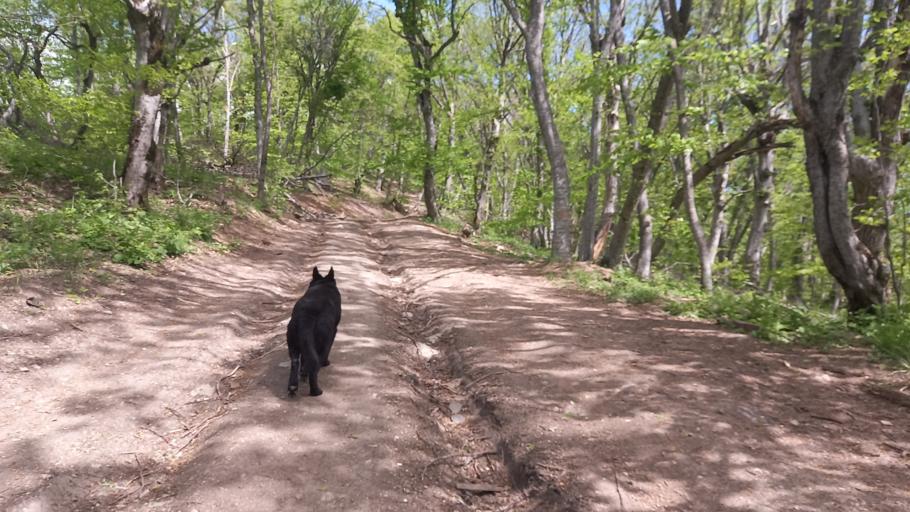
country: RU
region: Stavropol'skiy
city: Pyatigorsk
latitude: 44.0865
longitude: 43.0297
